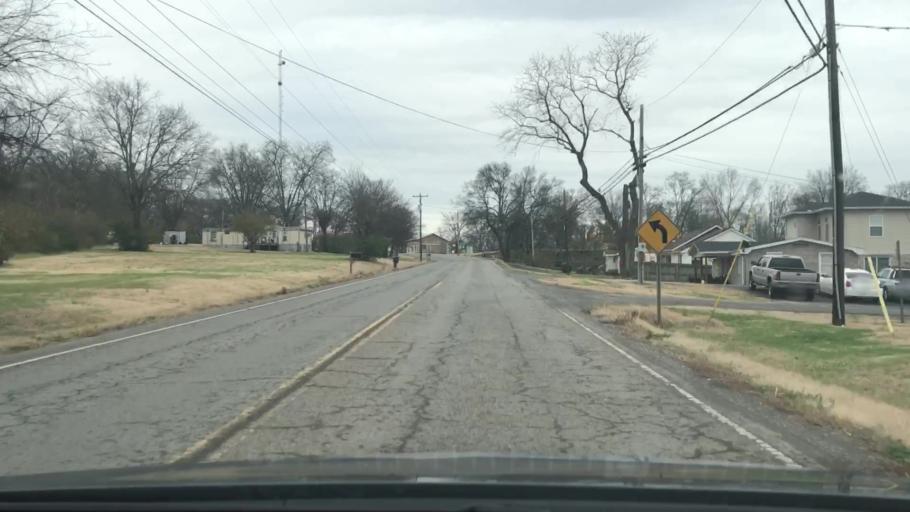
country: US
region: Tennessee
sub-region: Sumner County
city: Gallatin
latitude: 36.4074
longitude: -86.4520
